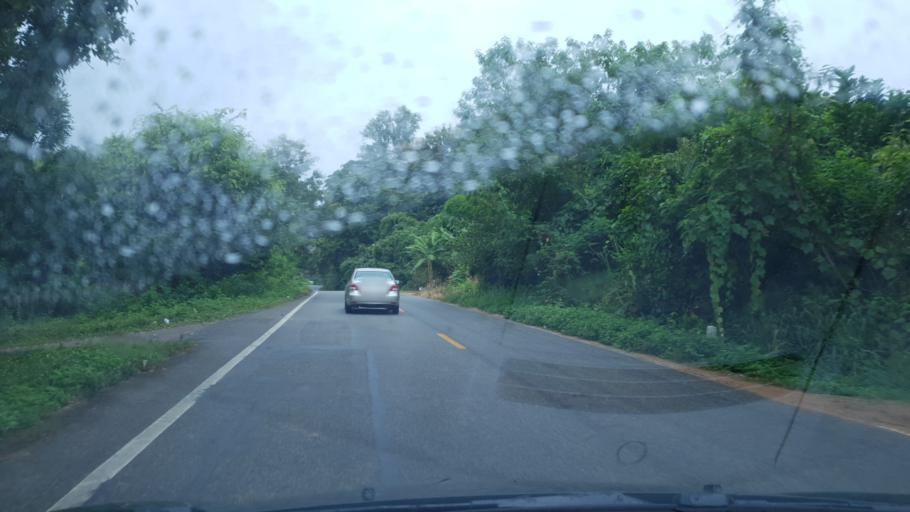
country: TH
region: Mae Hong Son
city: Khun Yuam
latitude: 18.7013
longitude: 97.9170
